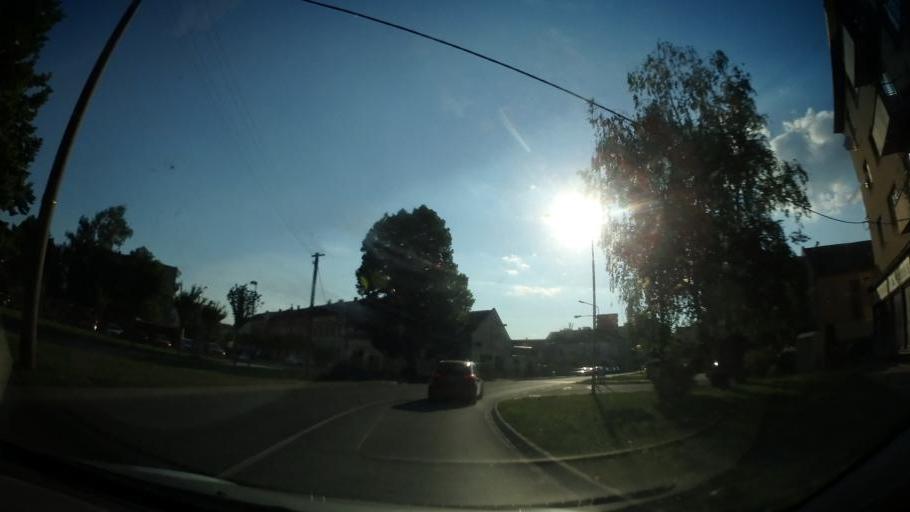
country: CZ
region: South Moravian
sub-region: Okres Vyskov
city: Vyskov
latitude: 49.2808
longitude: 17.0040
